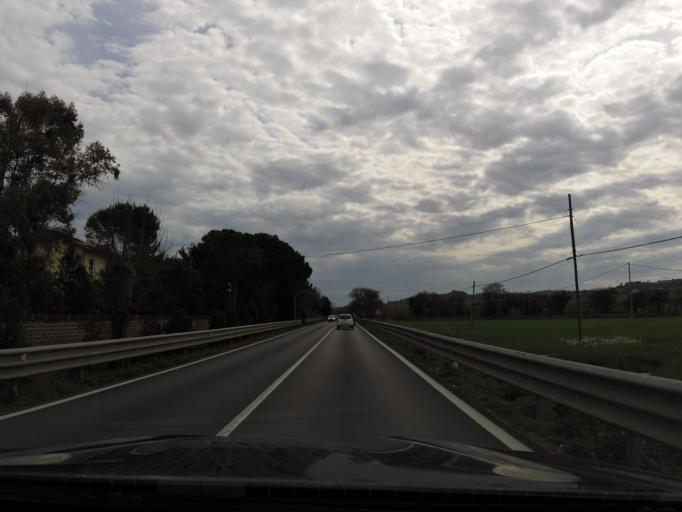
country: IT
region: The Marches
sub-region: Provincia di Macerata
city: Porto Recanati
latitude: 43.3969
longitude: 13.6791
